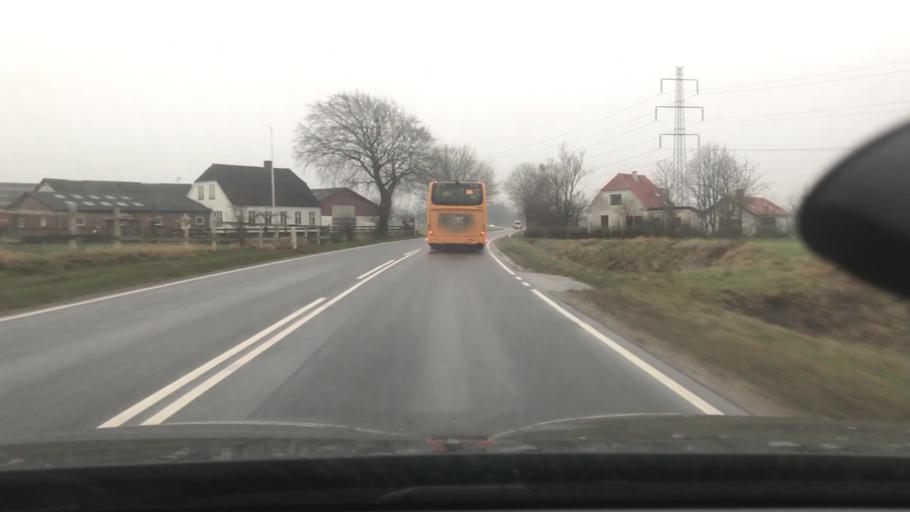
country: DK
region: Zealand
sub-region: Koge Kommune
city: Ejby
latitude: 55.5050
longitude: 12.1137
